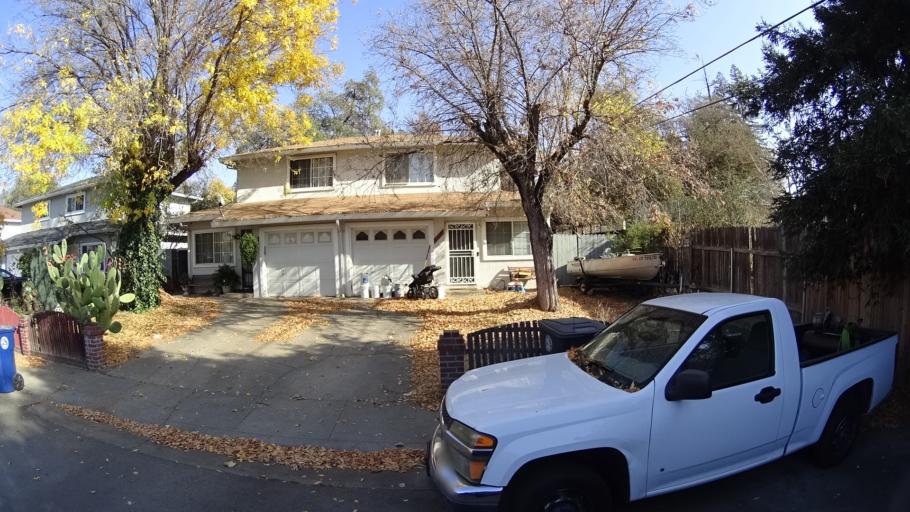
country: US
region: California
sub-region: Sacramento County
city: Citrus Heights
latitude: 38.6811
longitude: -121.2826
